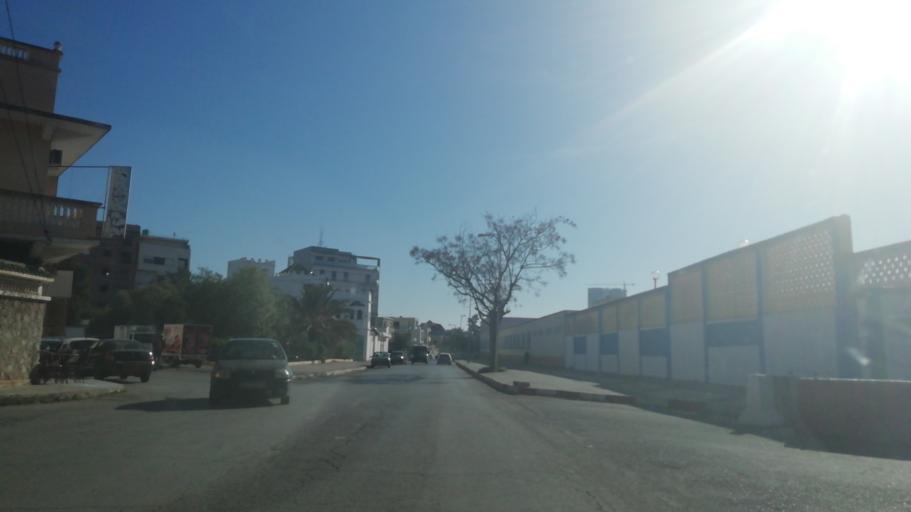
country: DZ
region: Oran
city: Oran
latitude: 35.6740
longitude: -0.6473
